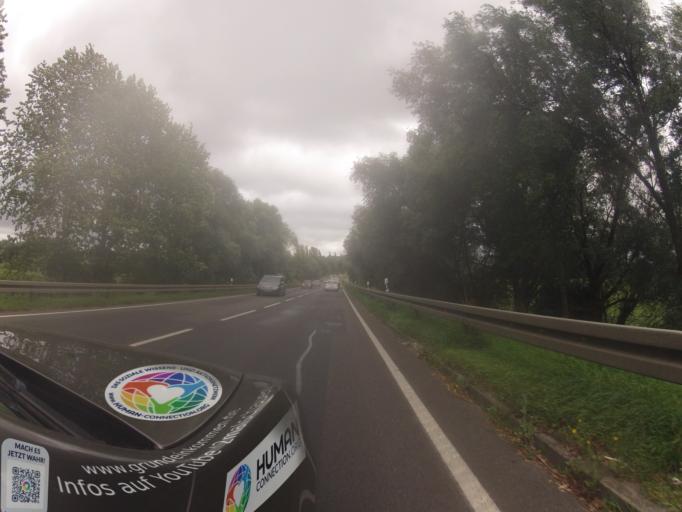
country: DE
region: Mecklenburg-Vorpommern
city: Pasewalk
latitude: 53.5034
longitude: 13.9802
